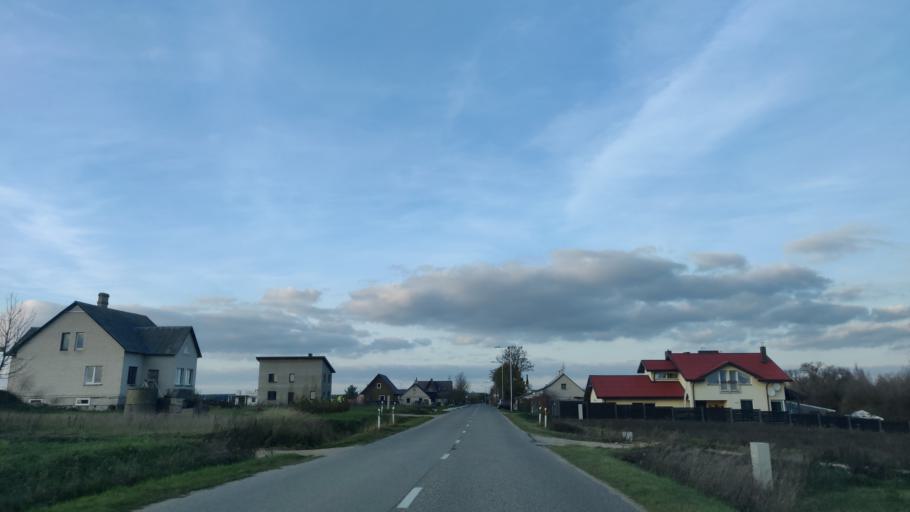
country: LT
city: Lentvaris
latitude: 54.5795
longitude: 25.0516
